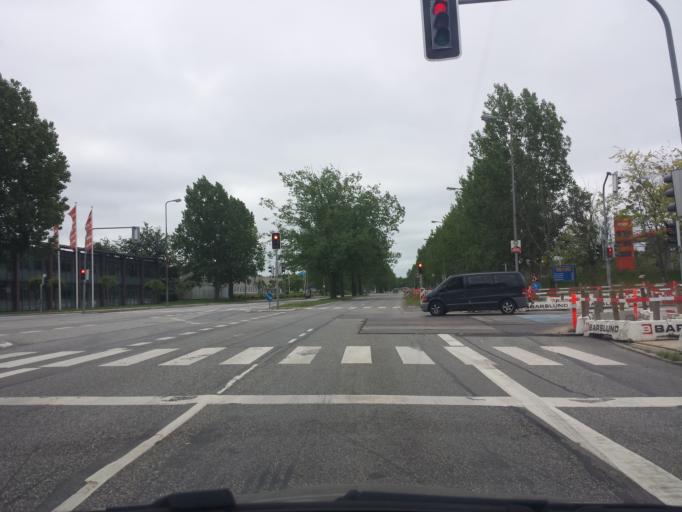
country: DK
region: Capital Region
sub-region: Herlev Kommune
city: Herlev
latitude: 55.6979
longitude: 12.4212
